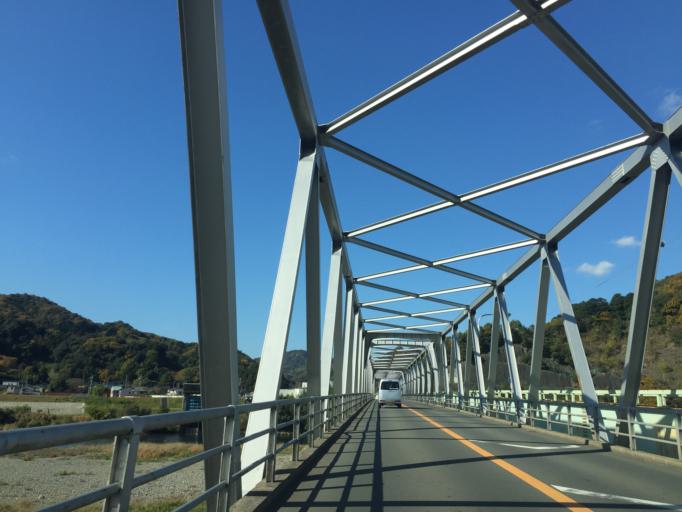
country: JP
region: Shizuoka
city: Mishima
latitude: 35.0199
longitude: 138.9388
